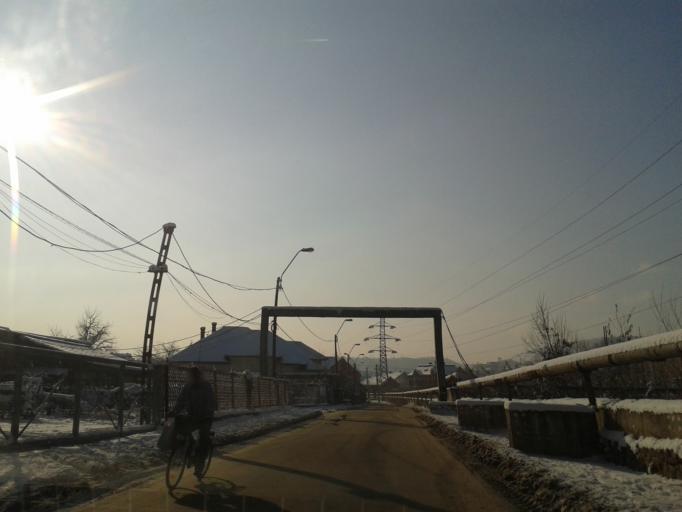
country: RO
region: Hunedoara
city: Hunedoara
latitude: 45.7544
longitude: 22.8954
